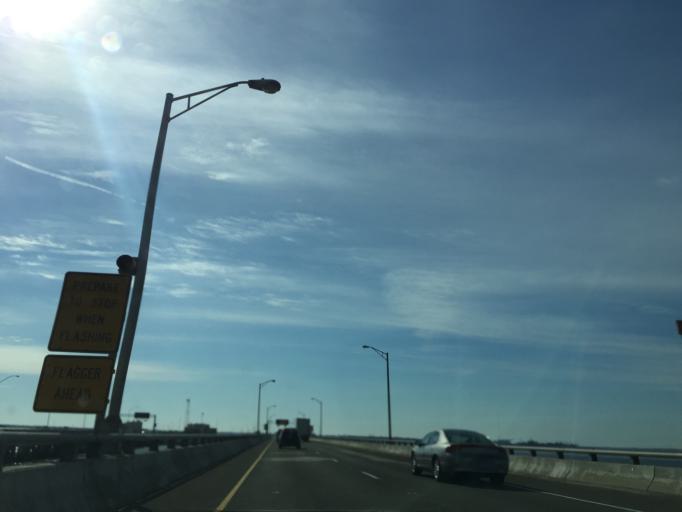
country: US
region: Virginia
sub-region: City of Hampton
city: East Hampton
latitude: 37.0061
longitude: -76.3211
